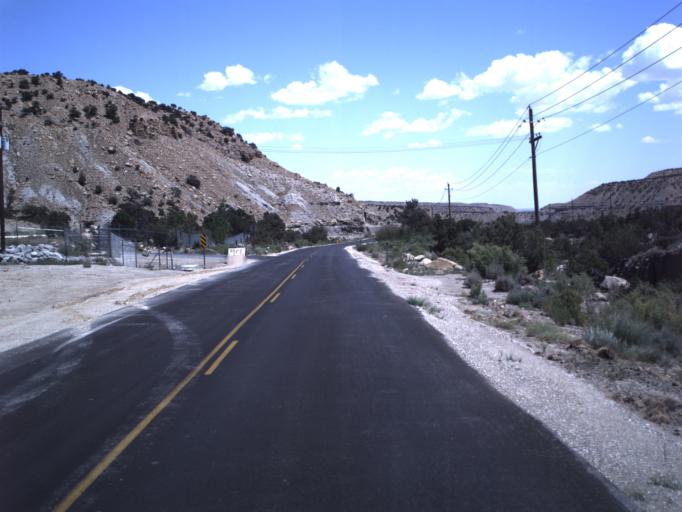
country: US
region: Utah
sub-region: Emery County
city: Orangeville
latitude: 39.2703
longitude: -111.1533
